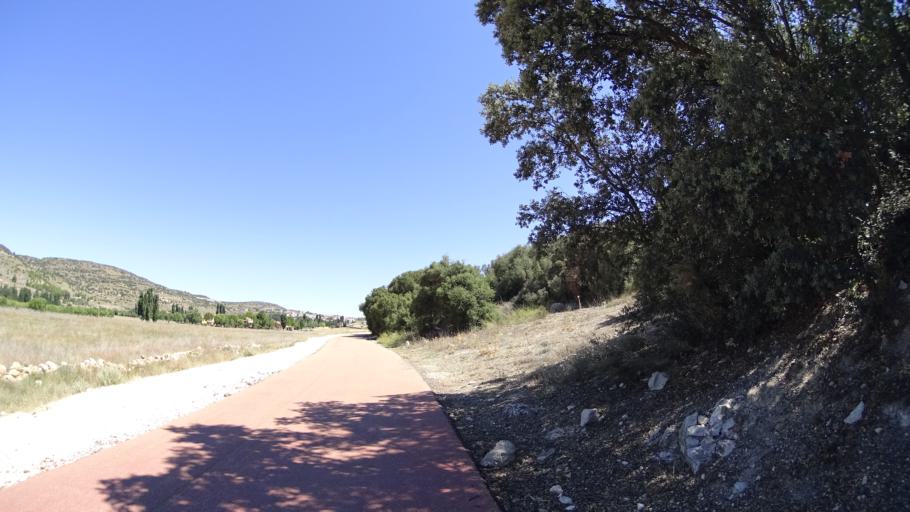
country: ES
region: Madrid
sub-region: Provincia de Madrid
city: Carabana
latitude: 40.2664
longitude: -3.2205
